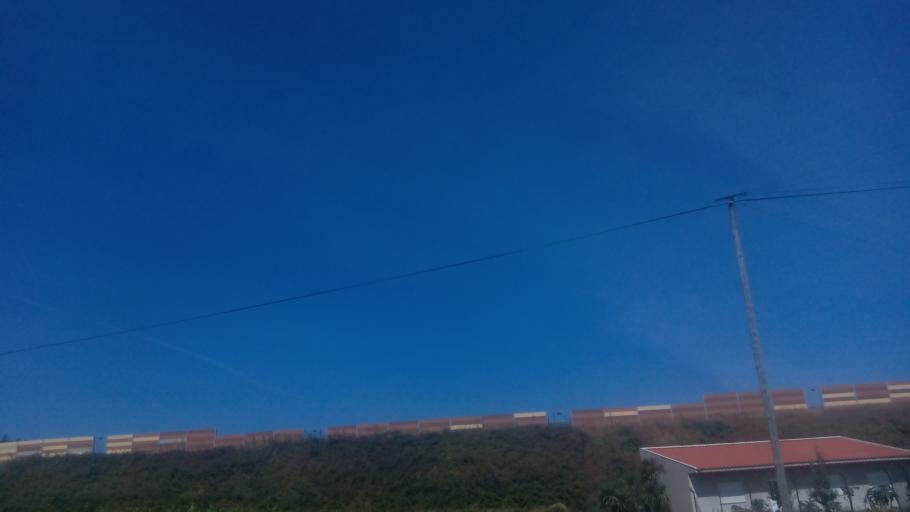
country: PT
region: Porto
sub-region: Paredes
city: Casteloes de Cepeda
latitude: 41.1965
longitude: -8.3312
